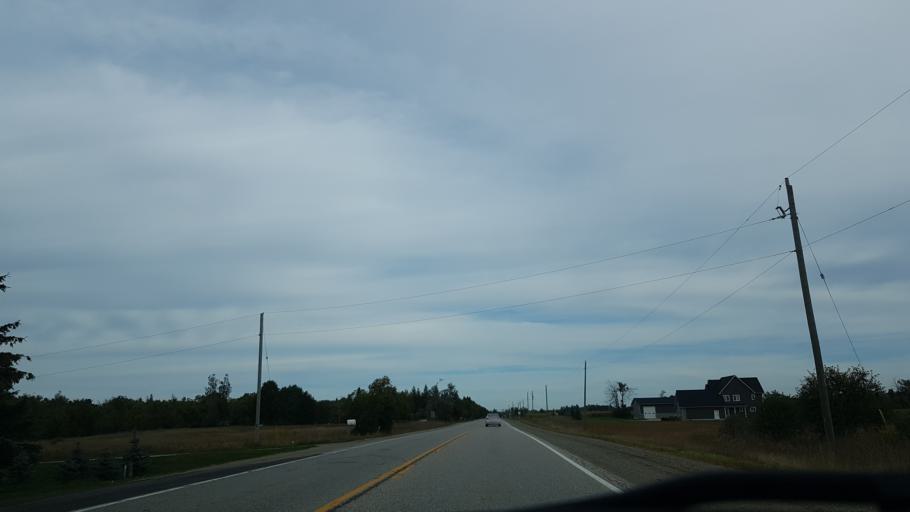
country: CA
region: Ontario
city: Orangeville
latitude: 43.7384
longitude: -80.0851
